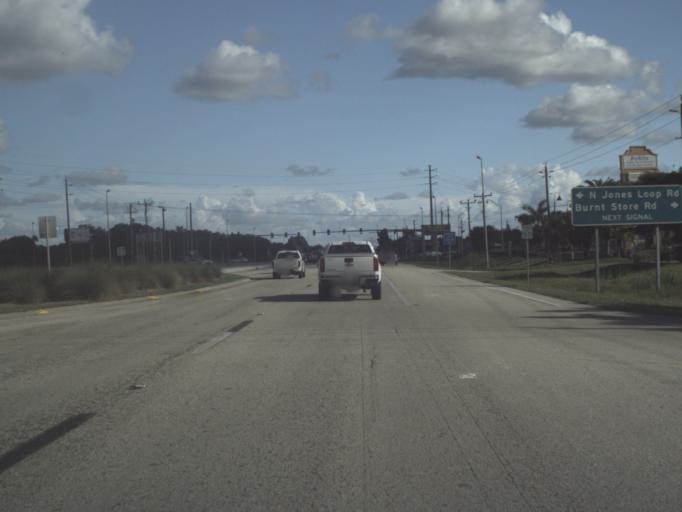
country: US
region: Florida
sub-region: Charlotte County
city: Charlotte Park
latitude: 26.8928
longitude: -82.0252
